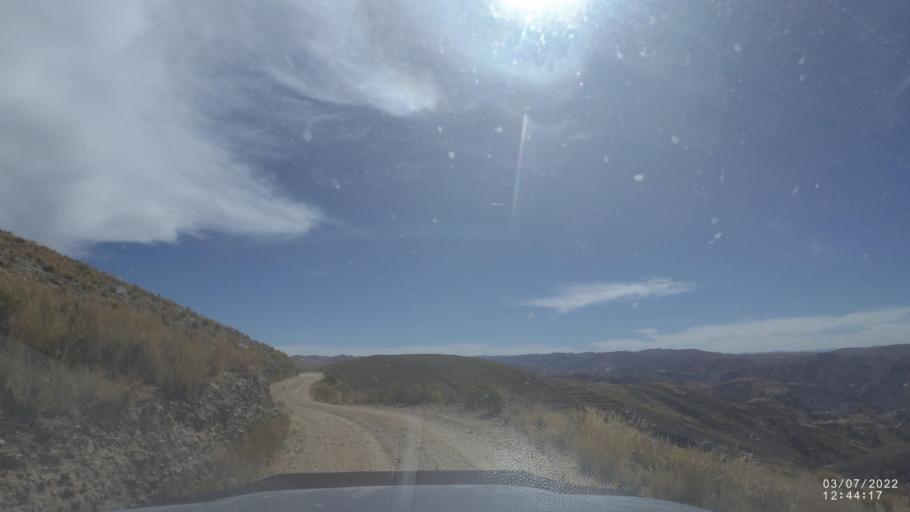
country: BO
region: Cochabamba
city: Irpa Irpa
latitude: -17.7801
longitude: -66.6321
